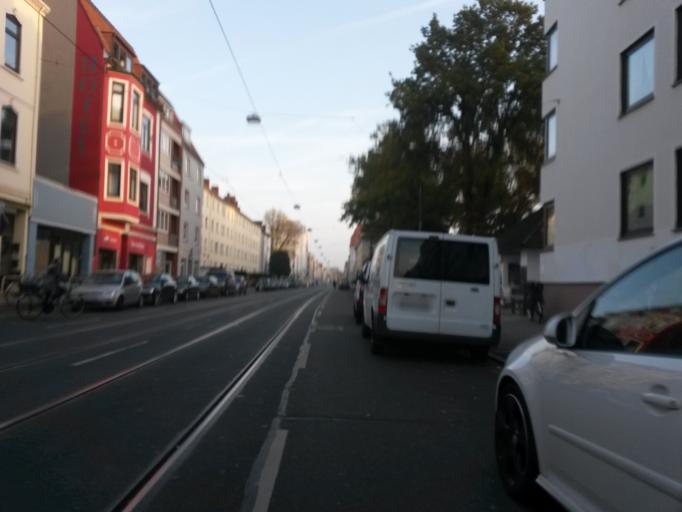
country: DE
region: Bremen
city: Bremen
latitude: 53.0667
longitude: 8.8037
